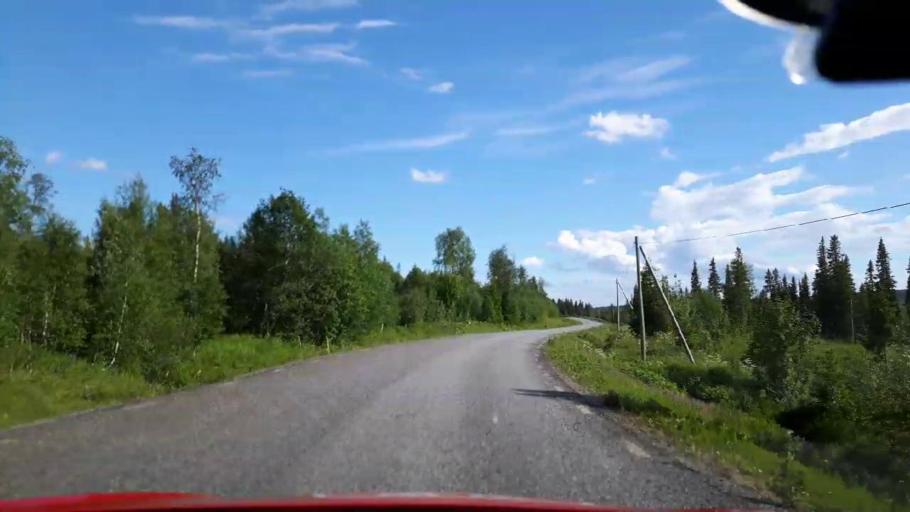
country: SE
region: Jaemtland
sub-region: Krokoms Kommun
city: Valla
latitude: 63.7094
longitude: 14.1415
